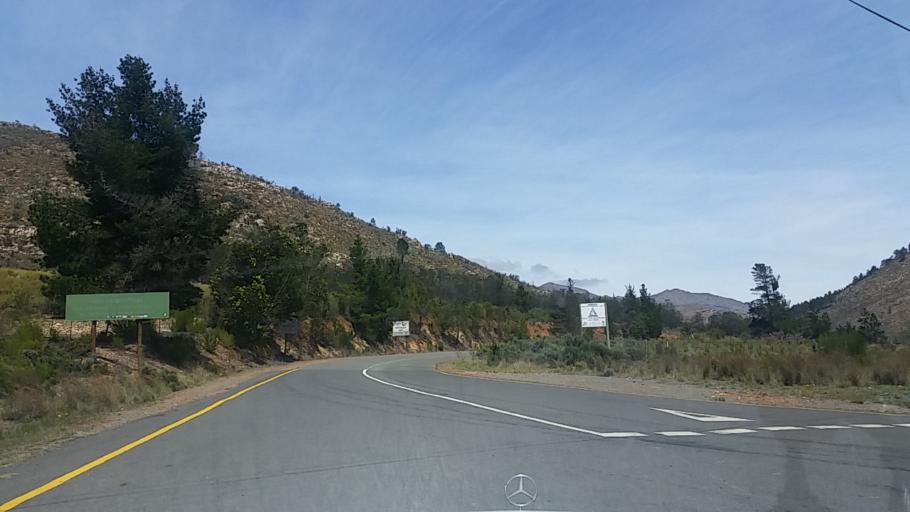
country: ZA
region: Western Cape
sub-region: Eden District Municipality
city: George
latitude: -33.8343
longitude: 22.4484
